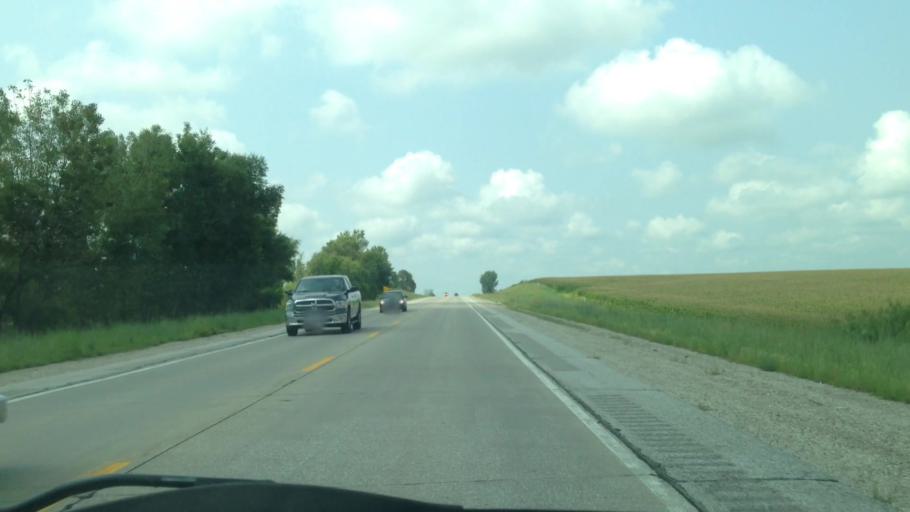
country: US
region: Iowa
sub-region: Linn County
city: Fairfax
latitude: 41.9007
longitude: -91.8032
